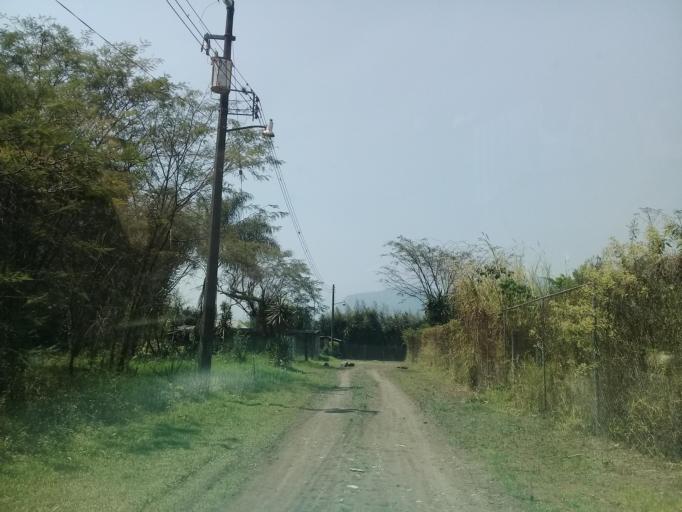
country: MX
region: Veracruz
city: Ixtac Zoquitlan
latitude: 18.8644
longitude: -97.0416
